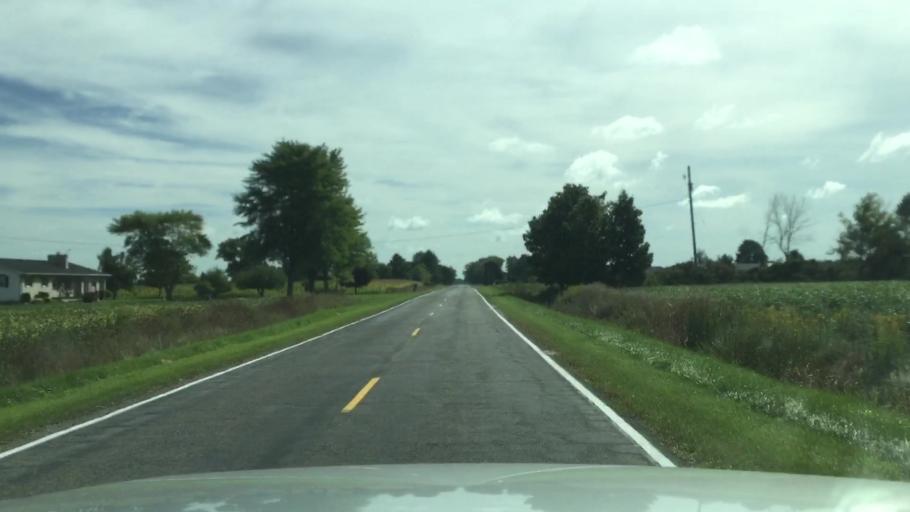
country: US
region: Michigan
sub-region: Genesee County
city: Montrose
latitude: 43.1466
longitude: -84.0043
